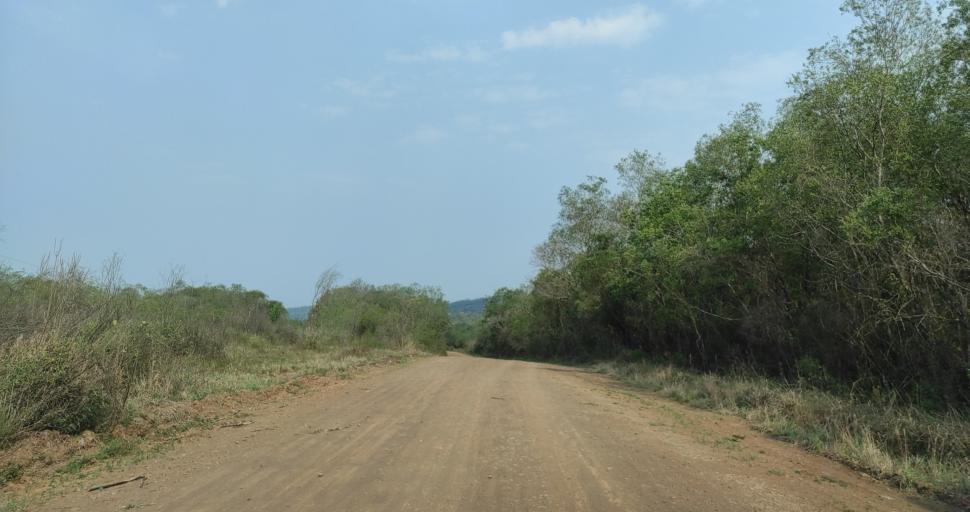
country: AR
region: Misiones
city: Cerro Cora
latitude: -27.5883
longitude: -55.5801
